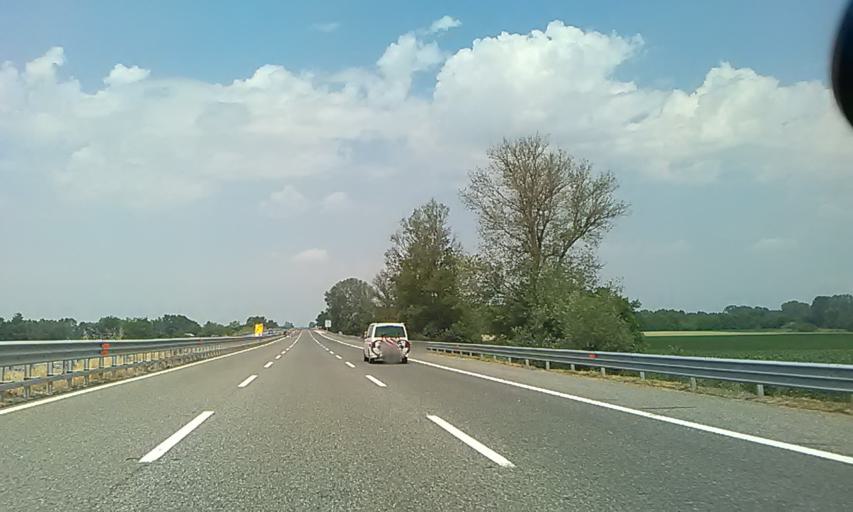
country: IT
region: Piedmont
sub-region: Provincia di Alessandria
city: Castellazzo Bormida
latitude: 44.8558
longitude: 8.5873
